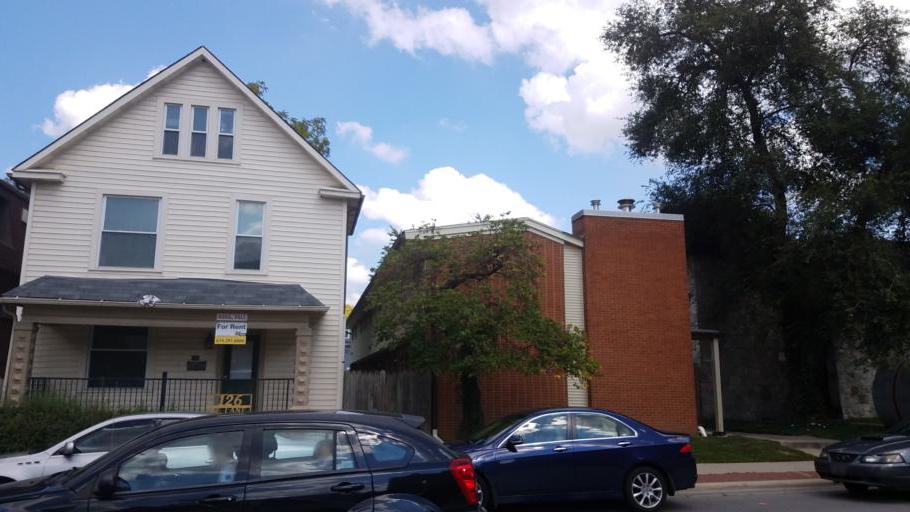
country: US
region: Ohio
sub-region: Franklin County
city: Grandview Heights
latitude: 40.0061
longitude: -83.0126
